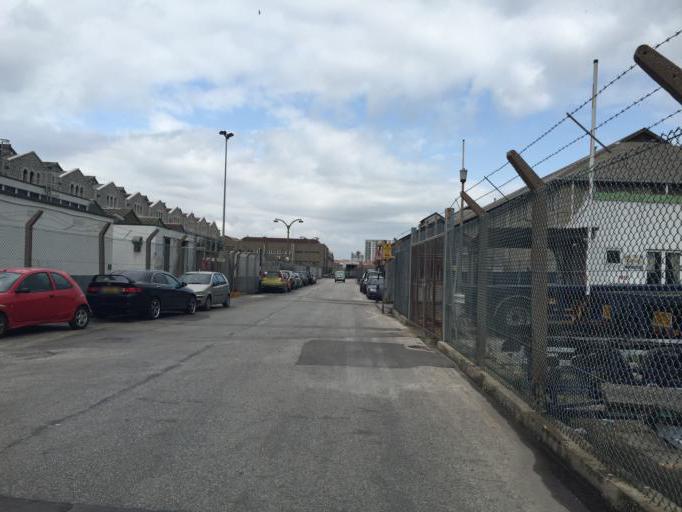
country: GI
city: Gibraltar
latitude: 36.1294
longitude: -5.3529
